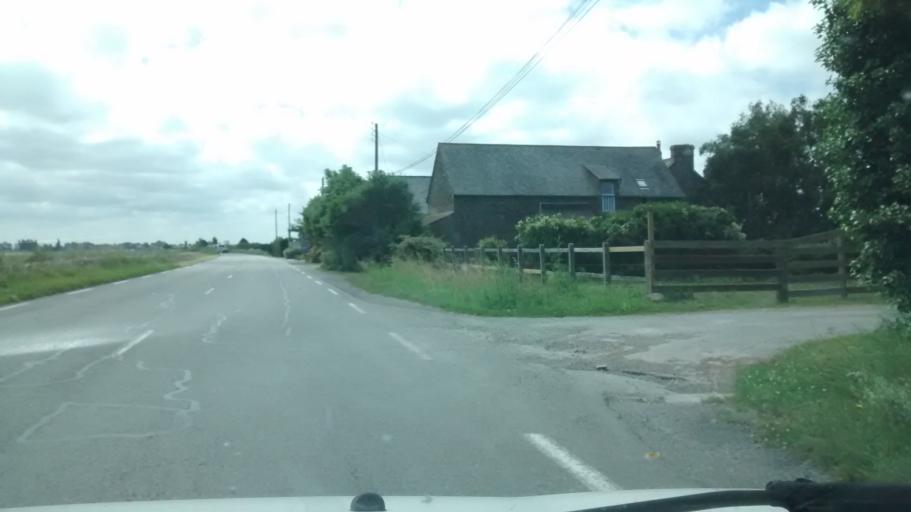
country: FR
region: Brittany
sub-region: Departement d'Ille-et-Vilaine
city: La Gouesniere
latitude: 48.6321
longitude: -1.8645
